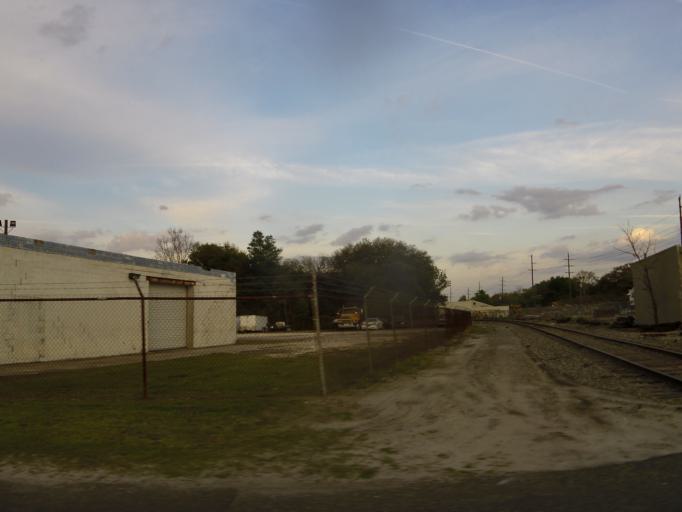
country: US
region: Florida
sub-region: Duval County
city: Jacksonville
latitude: 30.3631
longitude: -81.6329
